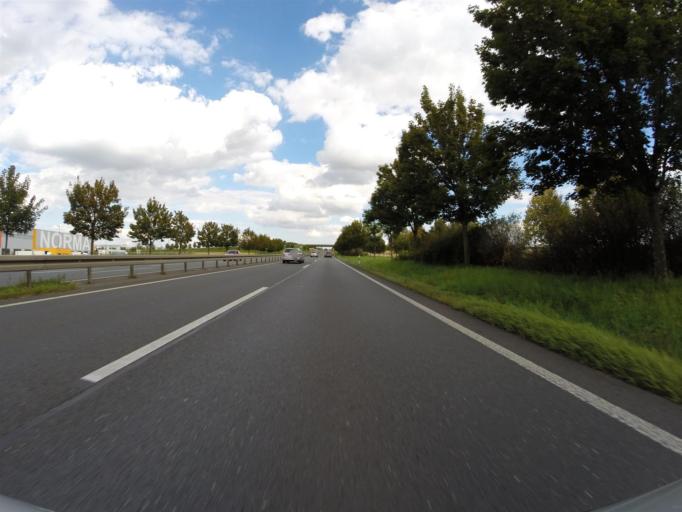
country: DE
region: Thuringia
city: Monchenholzhausen
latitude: 50.9750
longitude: 11.1206
